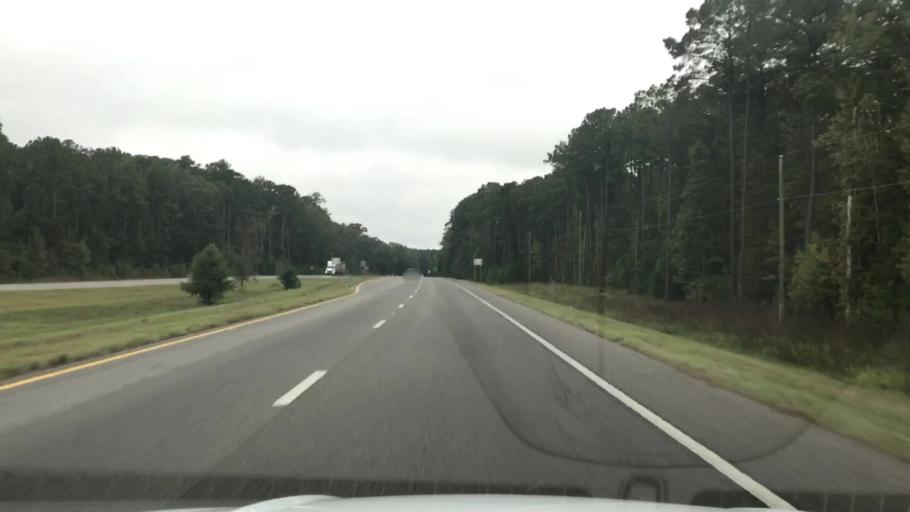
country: US
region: South Carolina
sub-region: Hampton County
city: Yemassee
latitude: 32.6690
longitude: -80.6497
